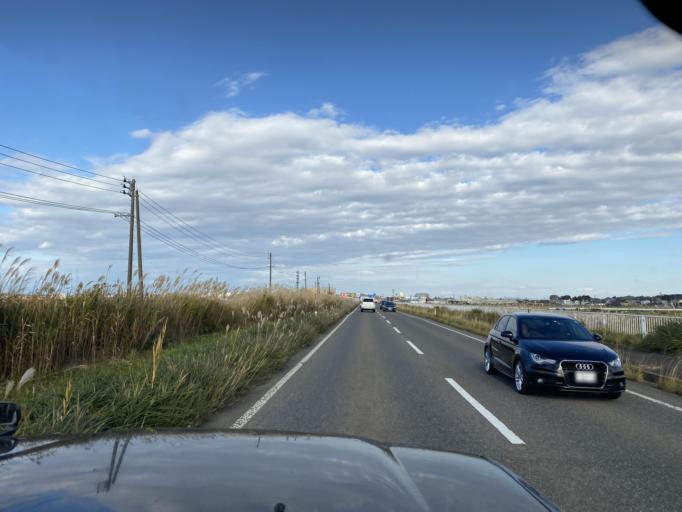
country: JP
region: Niigata
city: Niitsu-honcho
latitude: 37.7792
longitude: 139.1089
